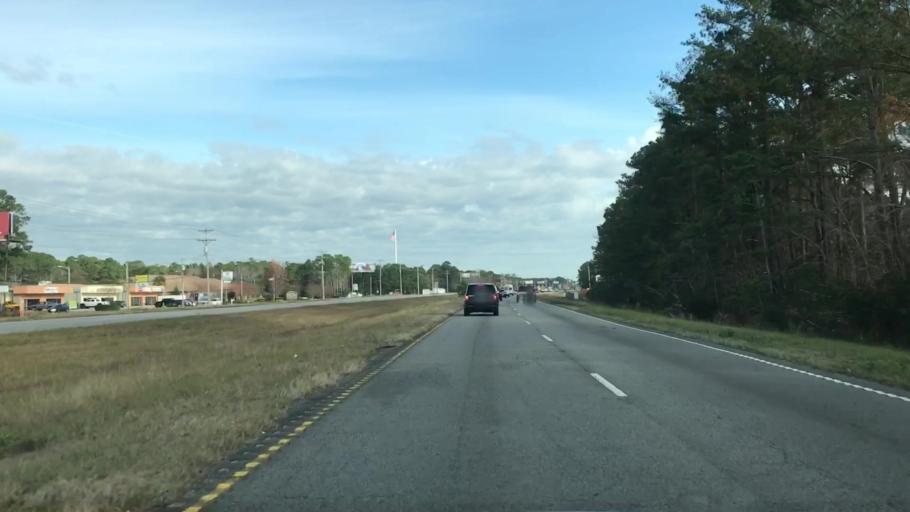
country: US
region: South Carolina
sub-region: Horry County
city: Garden City
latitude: 33.5949
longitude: -79.0239
